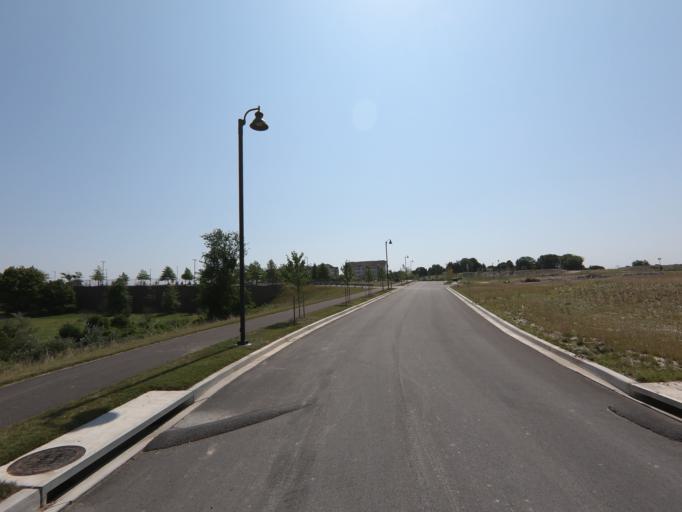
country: US
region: Maryland
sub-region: Frederick County
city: Spring Ridge
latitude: 39.3927
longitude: -77.3120
